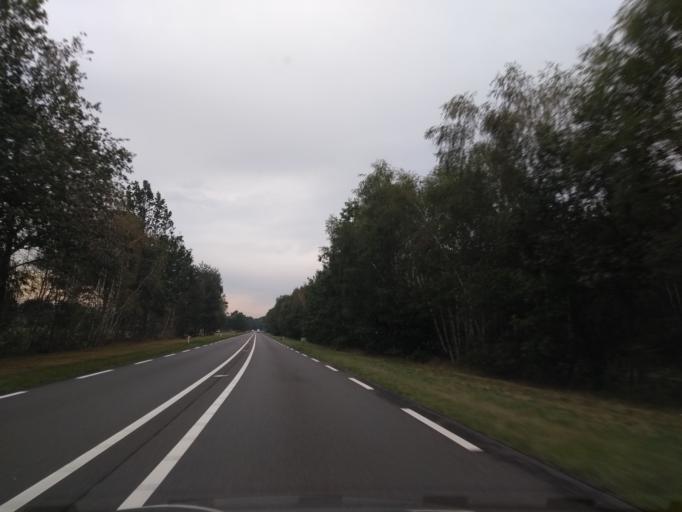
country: NL
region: Gelderland
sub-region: Oost Gelre
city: Lichtenvoorde
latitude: 52.0230
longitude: 6.6157
